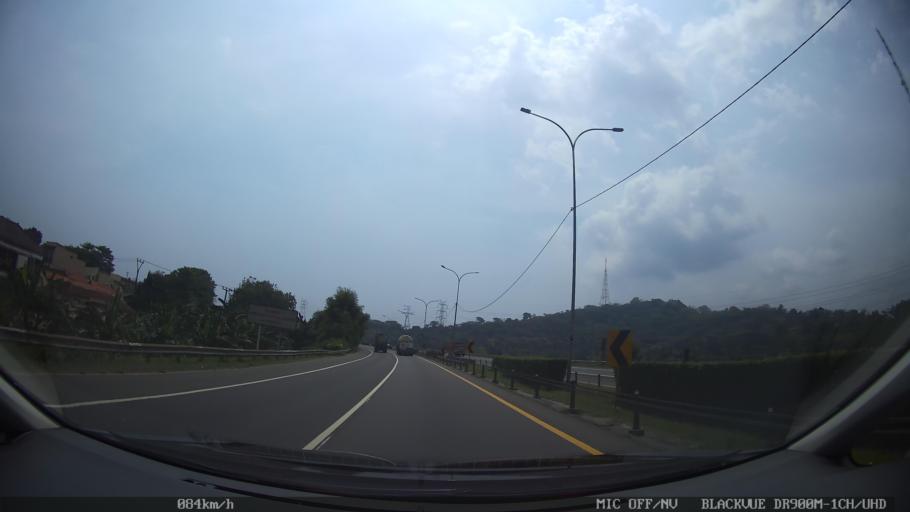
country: ID
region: Banten
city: Curug
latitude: -5.9907
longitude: 106.0501
